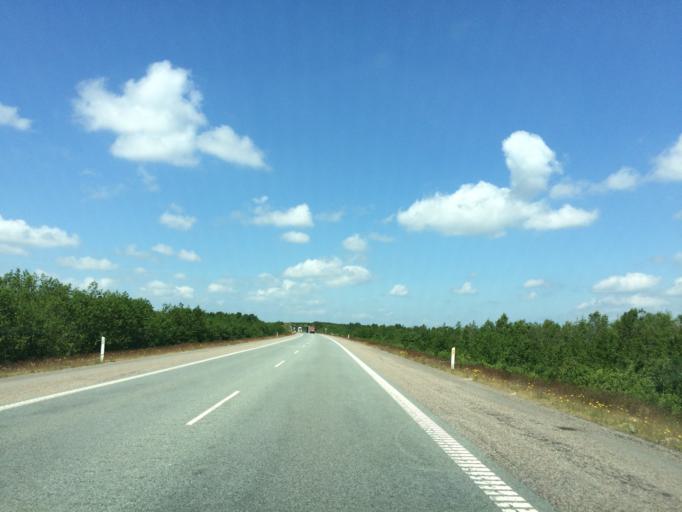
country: DK
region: Central Jutland
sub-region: Herning Kommune
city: Herning
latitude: 56.1743
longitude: 8.9889
